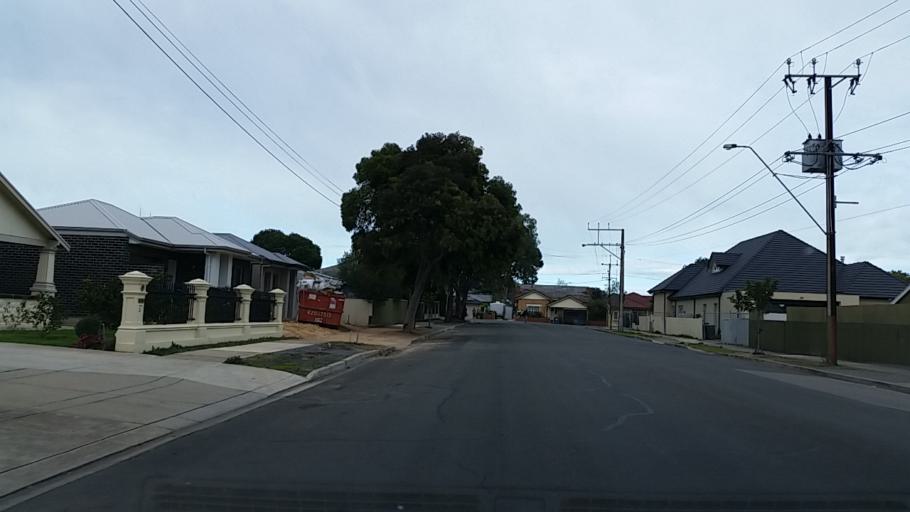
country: AU
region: South Australia
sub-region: Campbelltown
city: Hectorville
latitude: -34.9052
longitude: 138.6541
